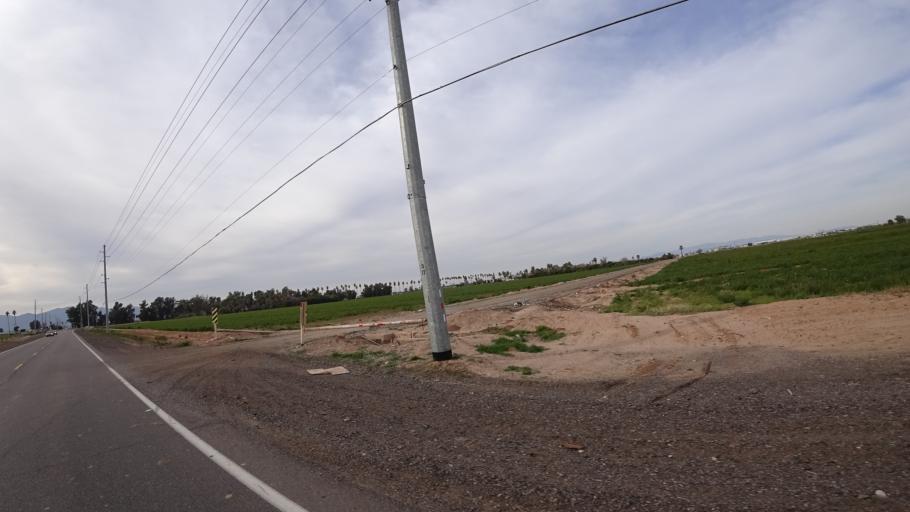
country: US
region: Arizona
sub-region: Maricopa County
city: El Mirage
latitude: 33.5657
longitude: -112.3543
